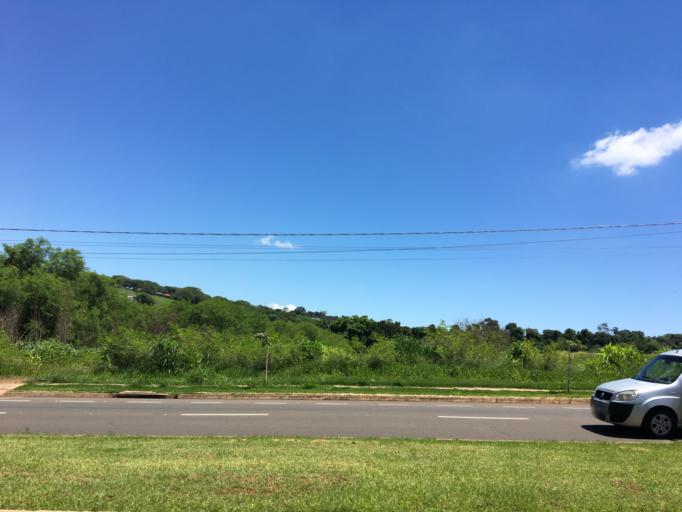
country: BR
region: Parana
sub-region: Maringa
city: Maringa
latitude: -23.4513
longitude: -51.9693
